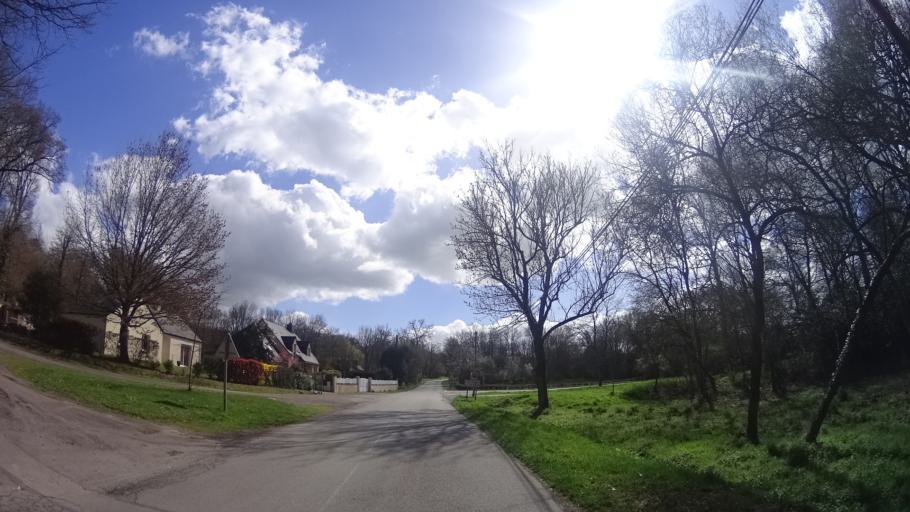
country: FR
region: Brittany
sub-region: Departement du Morbihan
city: Saint-Jean-la-Poterie
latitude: 47.6405
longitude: -2.1228
